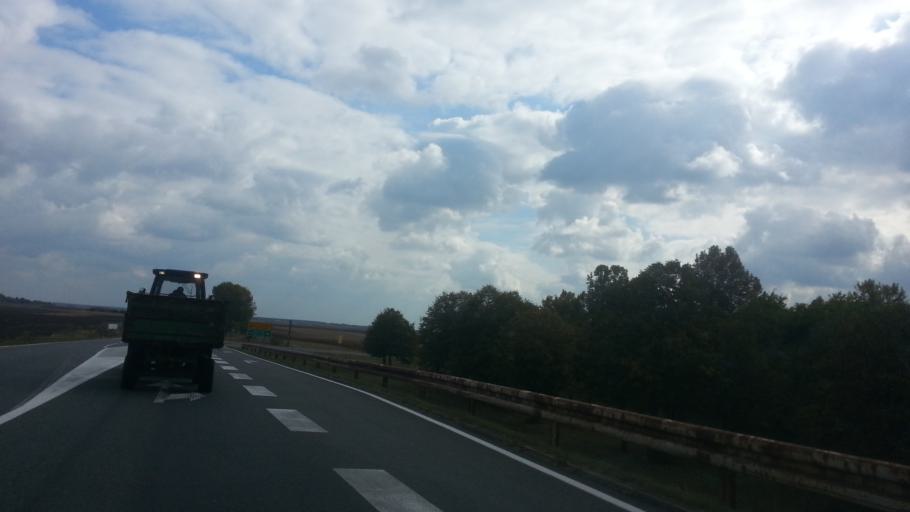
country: RS
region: Autonomna Pokrajina Vojvodina
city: Nova Pazova
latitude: 44.9866
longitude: 20.2179
